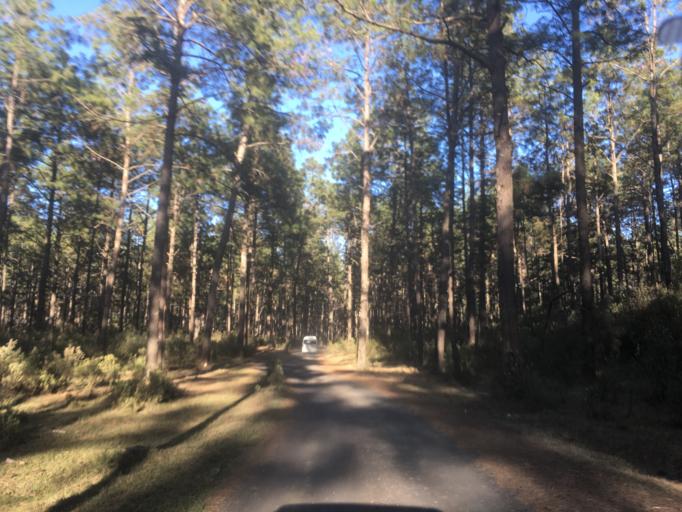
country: MX
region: Michoacan
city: Angahuan
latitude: 19.4636
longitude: -102.2305
